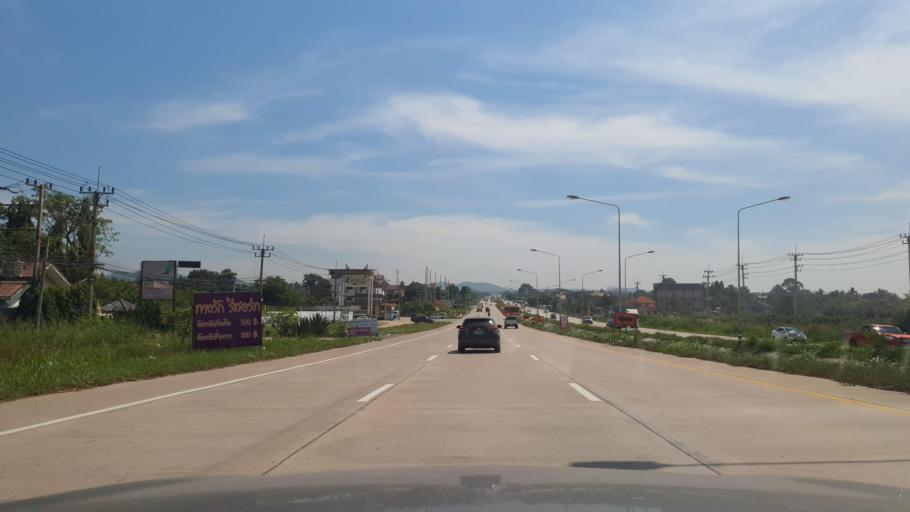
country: TH
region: Chon Buri
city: Bang Lamung
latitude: 12.9817
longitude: 100.9555
